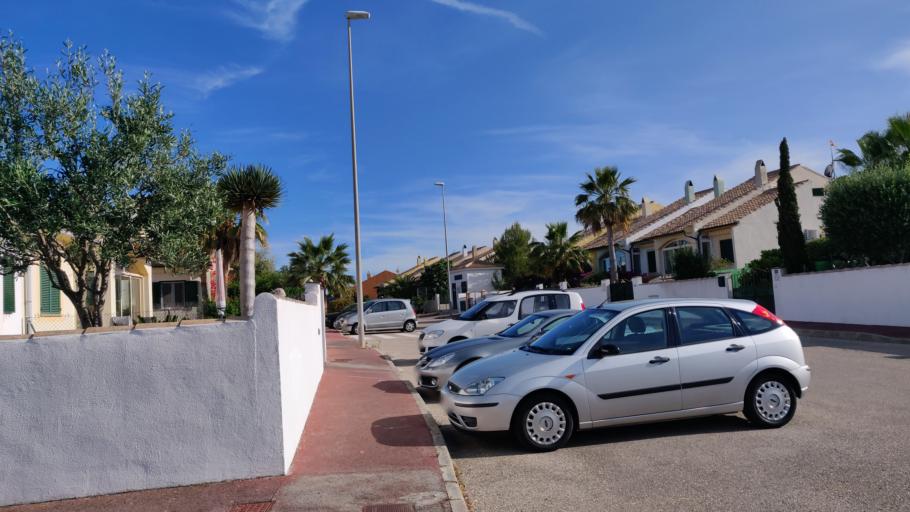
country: ES
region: Balearic Islands
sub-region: Illes Balears
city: Felanitx
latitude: 39.4529
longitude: 3.2602
